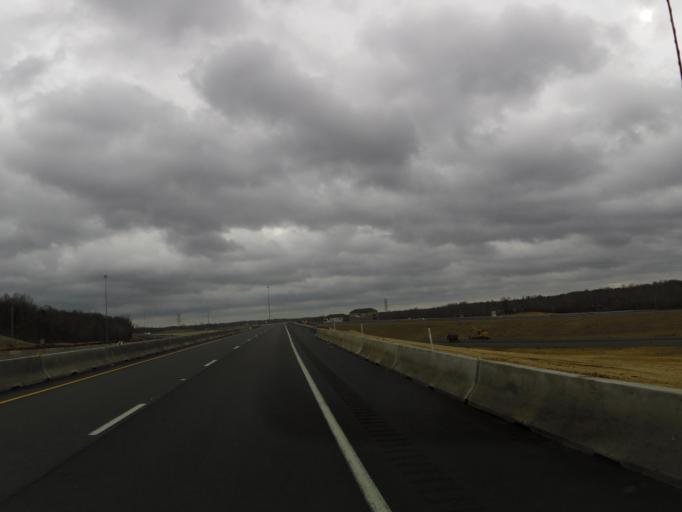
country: US
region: Kentucky
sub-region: Marshall County
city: Calvert City
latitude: 36.9908
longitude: -88.3435
